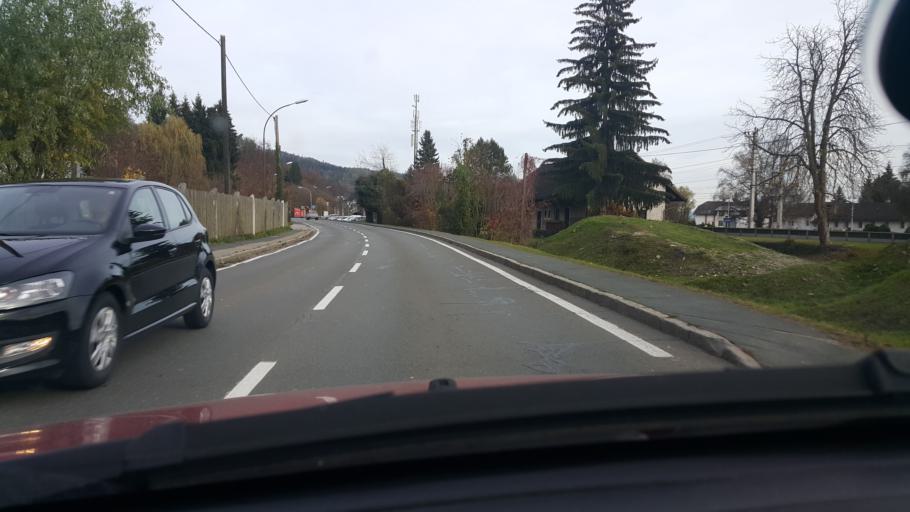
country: AT
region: Carinthia
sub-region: Politischer Bezirk Klagenfurt Land
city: Keutschach am See
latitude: 46.6262
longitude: 14.2192
